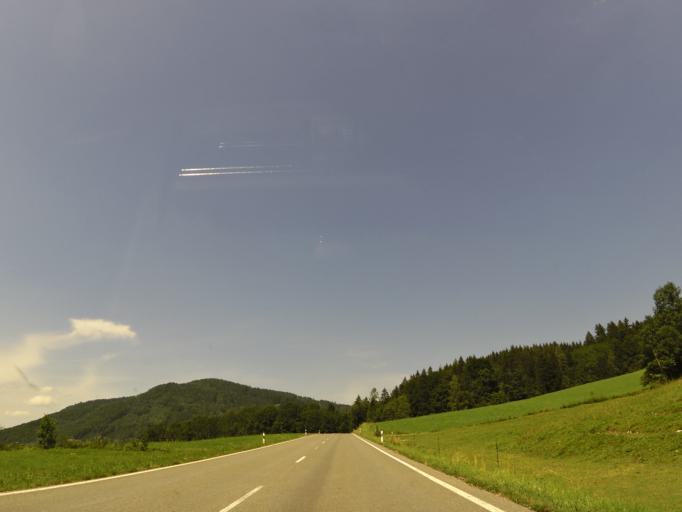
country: DE
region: Bavaria
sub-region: Upper Bavaria
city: Ruhpolding
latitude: 47.7434
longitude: 12.6704
